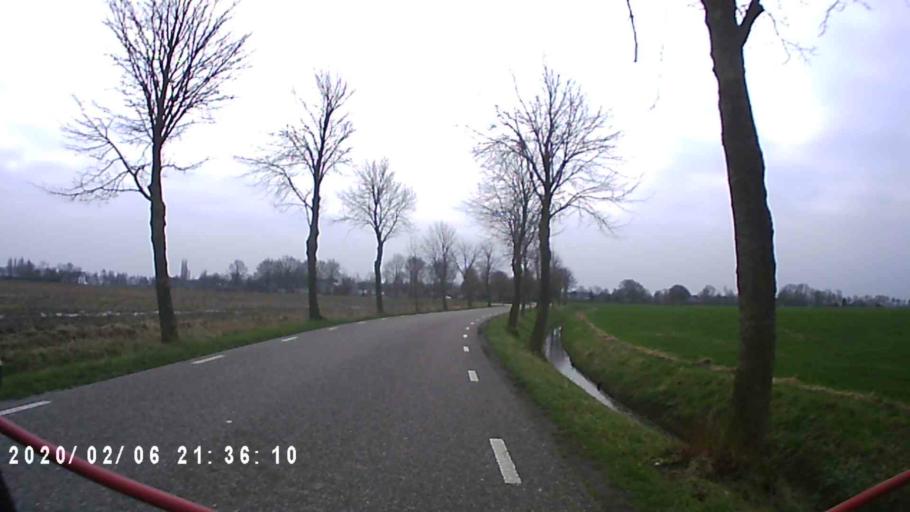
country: NL
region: Groningen
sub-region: Gemeente Zuidhorn
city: Noordhorn
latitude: 53.2683
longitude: 6.3940
